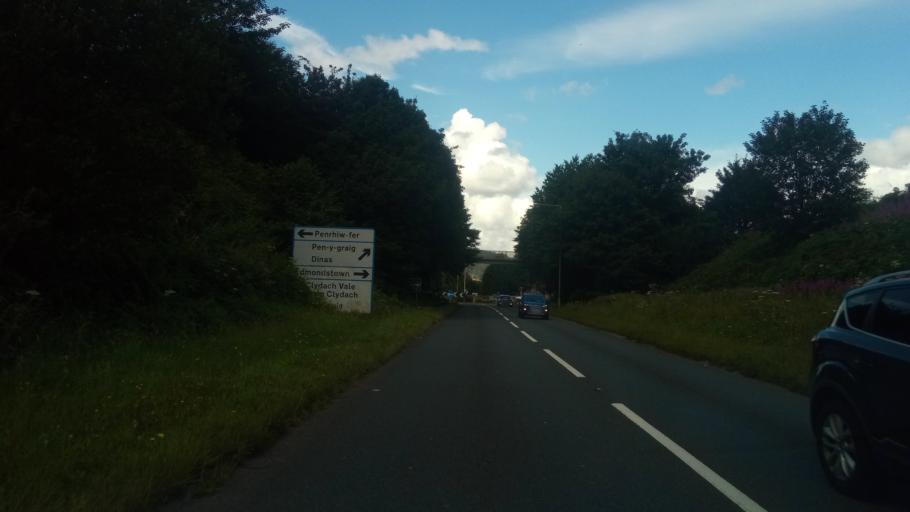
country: GB
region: Wales
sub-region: Rhondda Cynon Taf
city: Tonypandy
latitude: 51.6061
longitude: -3.4417
